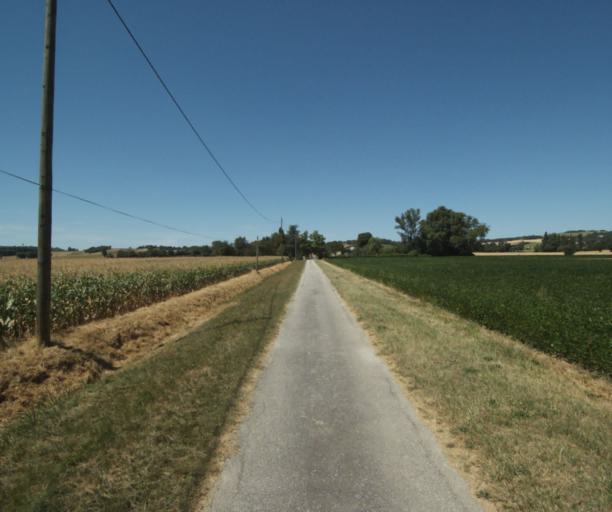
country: FR
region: Midi-Pyrenees
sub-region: Departement de la Haute-Garonne
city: Saint-Felix-Lauragais
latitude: 43.4826
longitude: 1.9360
